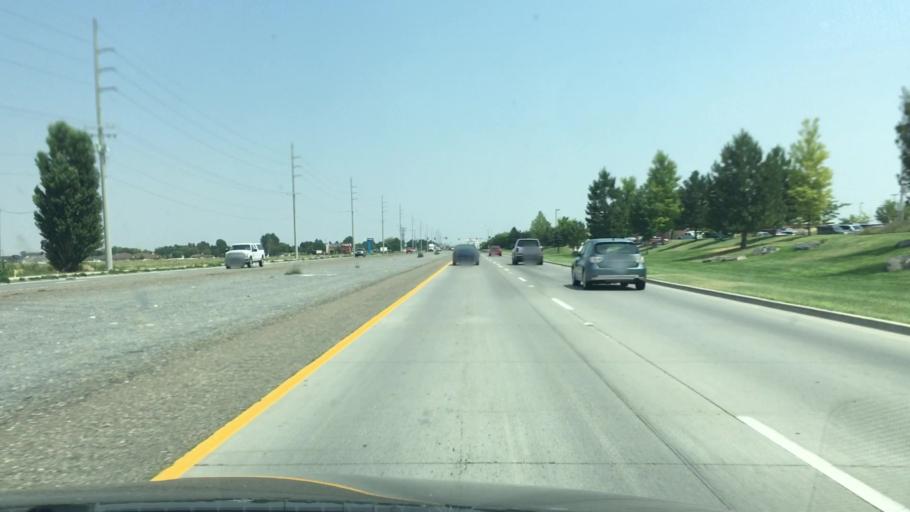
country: US
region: Idaho
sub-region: Twin Falls County
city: Twin Falls
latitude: 42.5916
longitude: -114.4956
